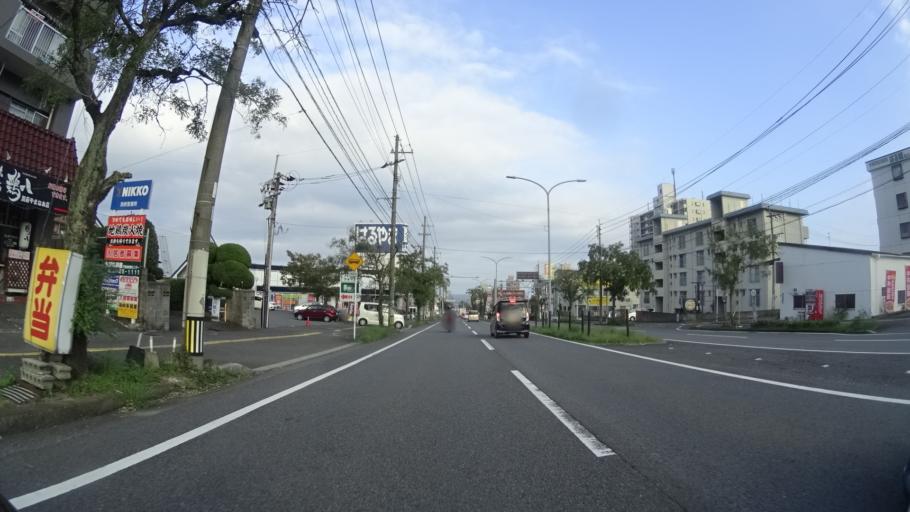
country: JP
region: Oita
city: Beppu
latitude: 33.3054
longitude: 131.4922
